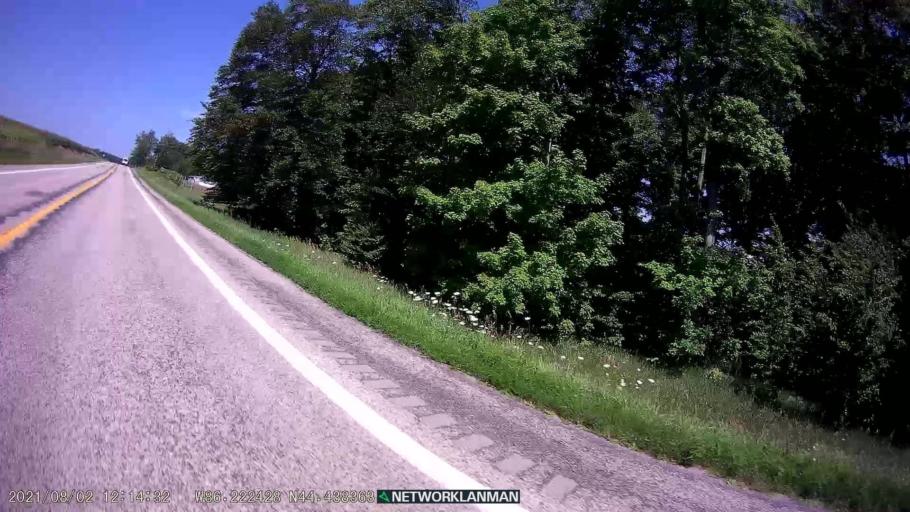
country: US
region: Michigan
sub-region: Benzie County
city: Frankfort
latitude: 44.4386
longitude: -86.2224
